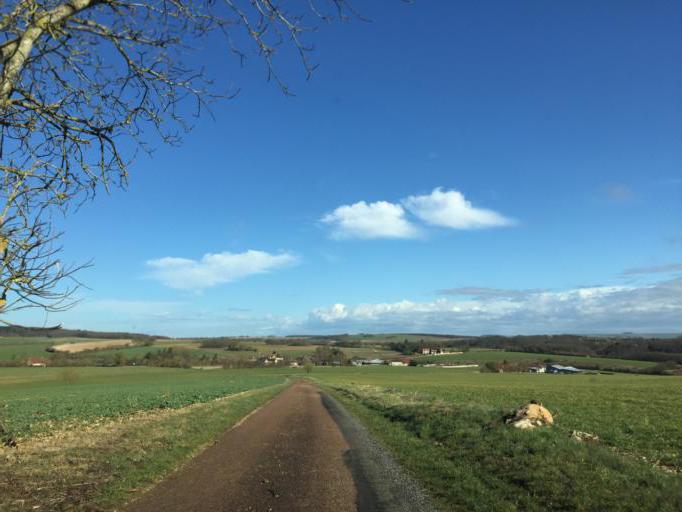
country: FR
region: Bourgogne
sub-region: Departement de l'Yonne
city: Fontenailles
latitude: 47.5518
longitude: 3.3305
